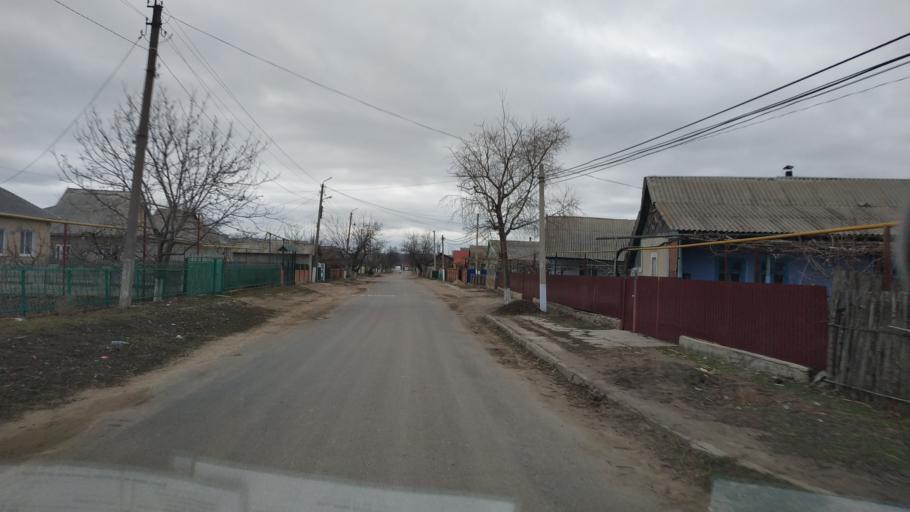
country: MD
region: Causeni
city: Causeni
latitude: 46.6642
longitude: 29.4873
